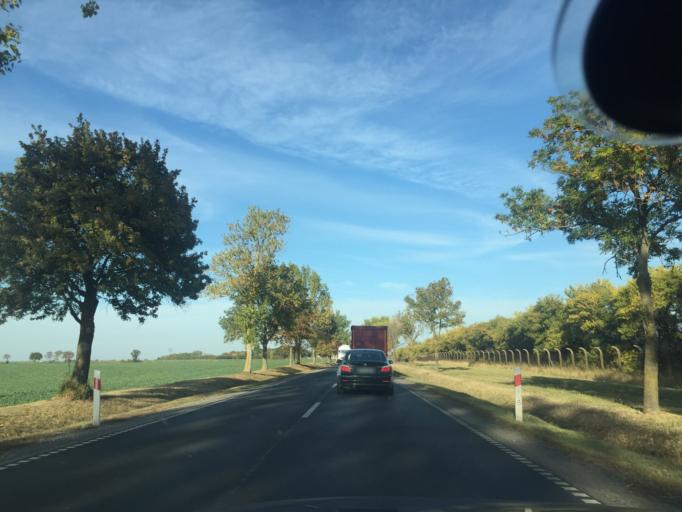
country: PL
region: Kujawsko-Pomorskie
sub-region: Powiat inowroclawski
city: Wierzchoslawice
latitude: 52.8356
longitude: 18.3196
